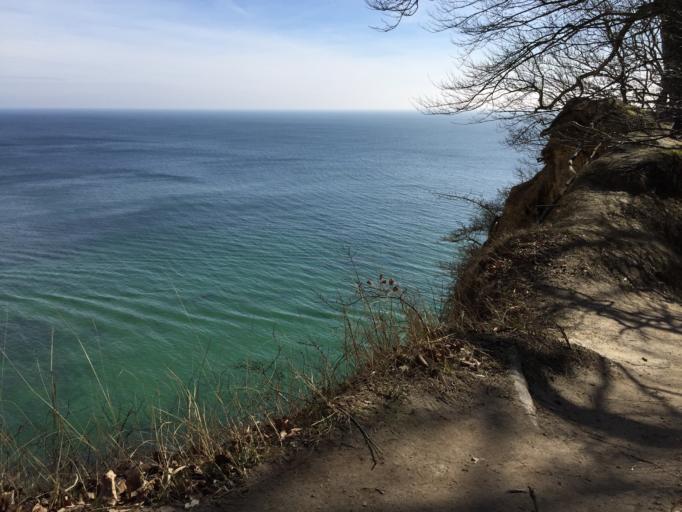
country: DE
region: Mecklenburg-Vorpommern
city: Sassnitz
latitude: 54.5258
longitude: 13.6707
